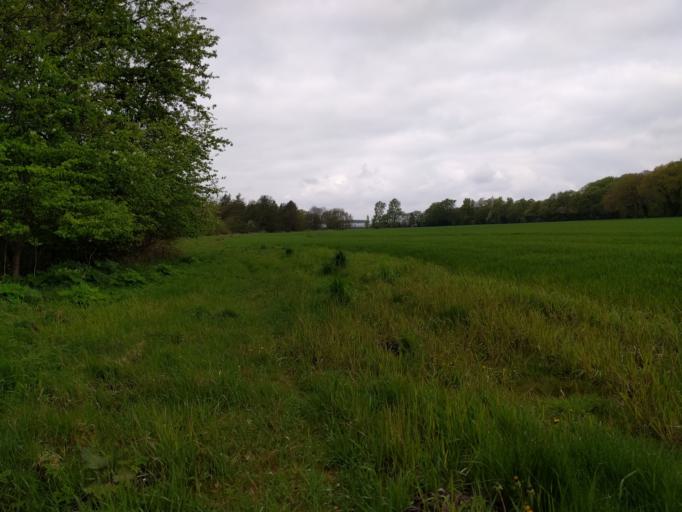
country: DK
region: South Denmark
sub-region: Kerteminde Kommune
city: Langeskov
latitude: 55.3958
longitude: 10.5758
